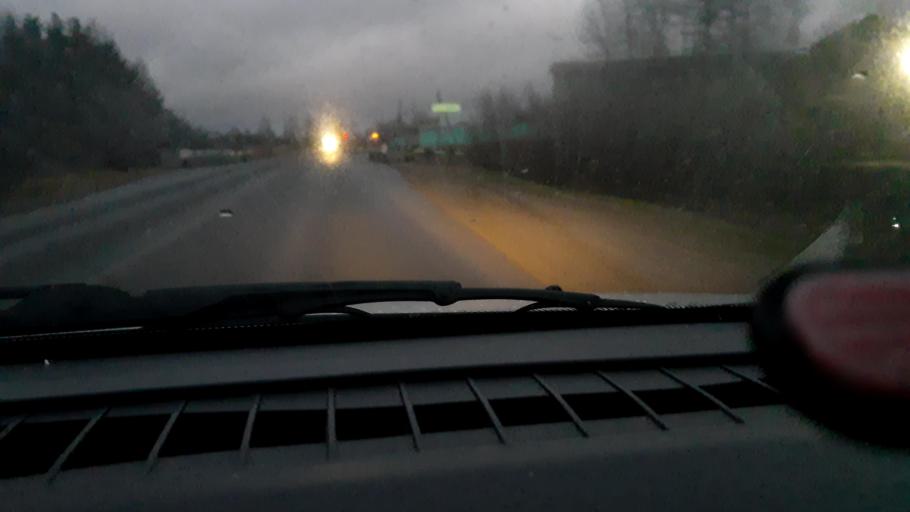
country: RU
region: Nizjnij Novgorod
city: Uren'
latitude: 57.4444
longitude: 45.7290
